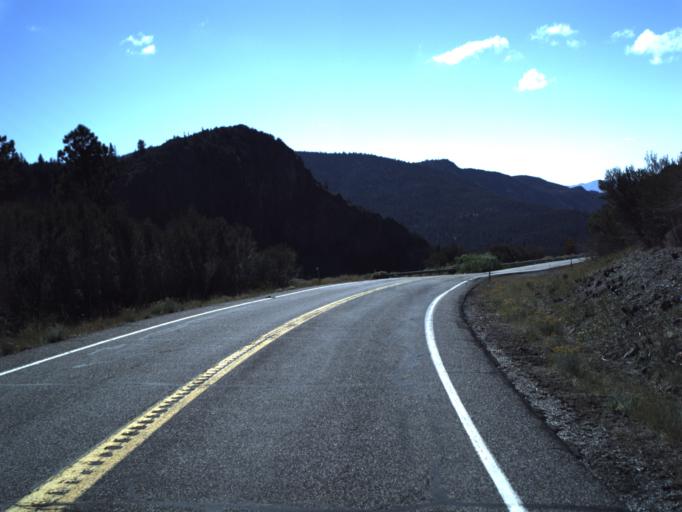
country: US
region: Utah
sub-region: Beaver County
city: Beaver
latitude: 38.2712
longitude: -112.4696
